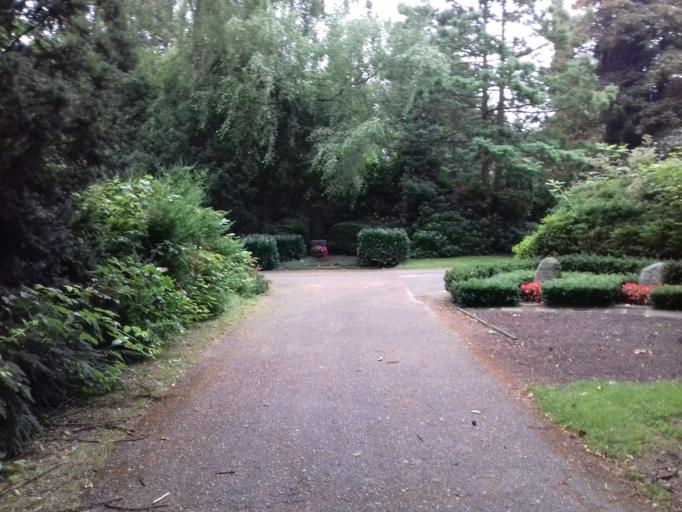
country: DE
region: Schleswig-Holstein
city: Neumunster
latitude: 54.0740
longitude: 10.0017
